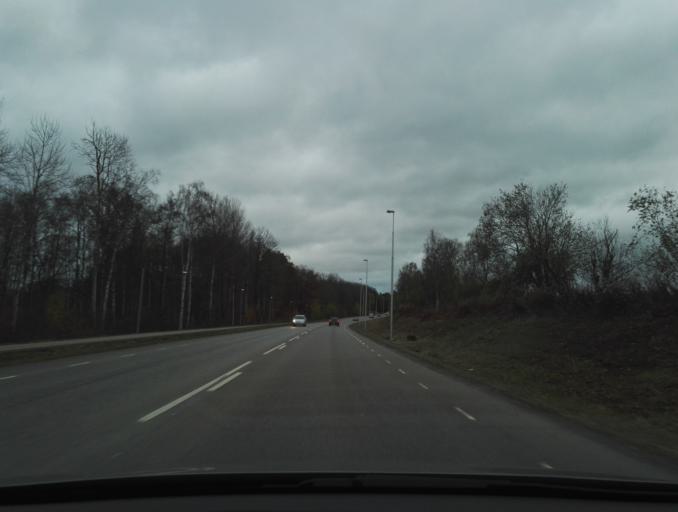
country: SE
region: Kronoberg
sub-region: Vaxjo Kommun
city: Vaexjoe
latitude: 56.8719
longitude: 14.7867
